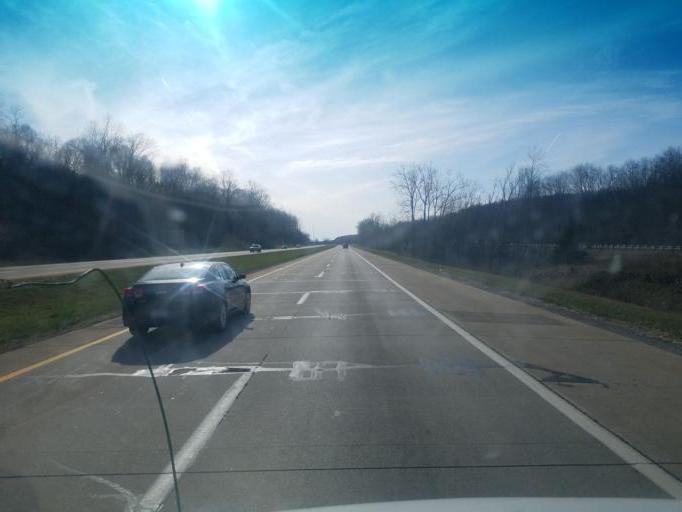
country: US
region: Ohio
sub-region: Champaign County
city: North Lewisburg
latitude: 40.3255
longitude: -83.6067
